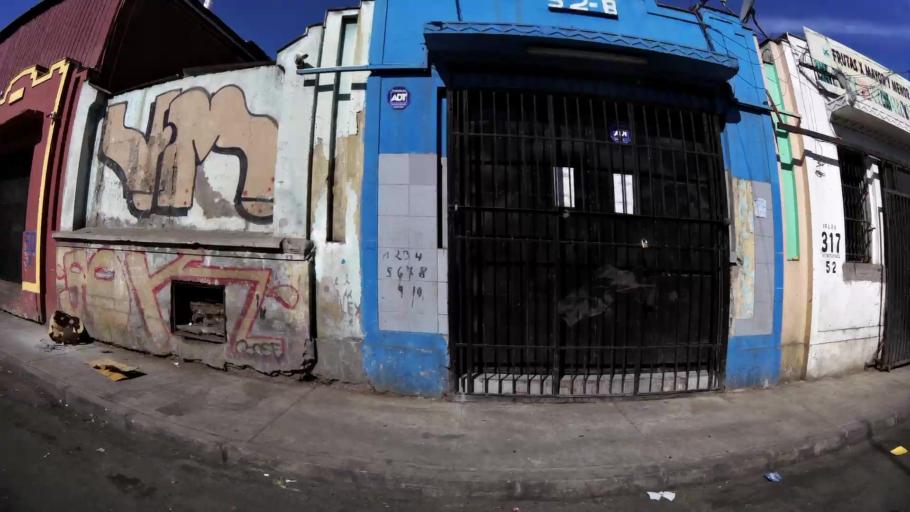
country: CL
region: Santiago Metropolitan
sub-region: Provincia de Santiago
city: Santiago
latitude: -33.4284
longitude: -70.6500
